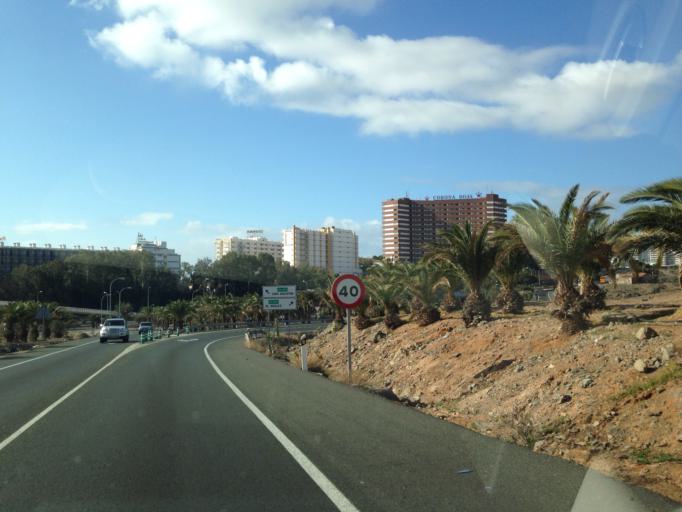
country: ES
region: Canary Islands
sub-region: Provincia de Las Palmas
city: Playa del Ingles
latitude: 27.7674
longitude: -15.5569
